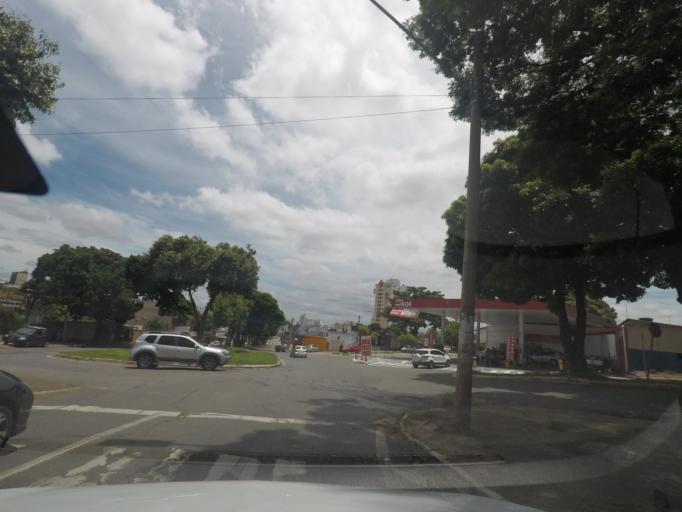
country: BR
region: Goias
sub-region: Goiania
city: Goiania
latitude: -16.6882
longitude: -49.2424
